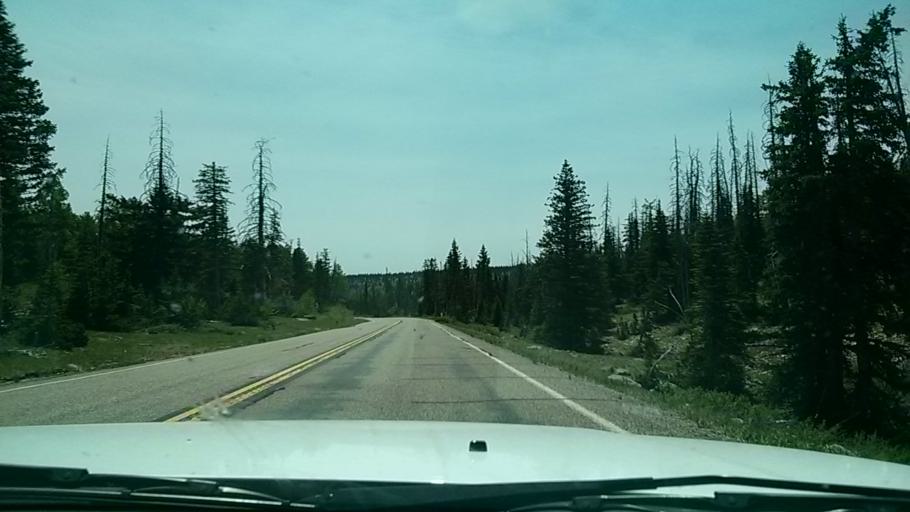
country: US
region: Utah
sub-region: Iron County
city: Cedar City
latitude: 37.5854
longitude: -112.8473
